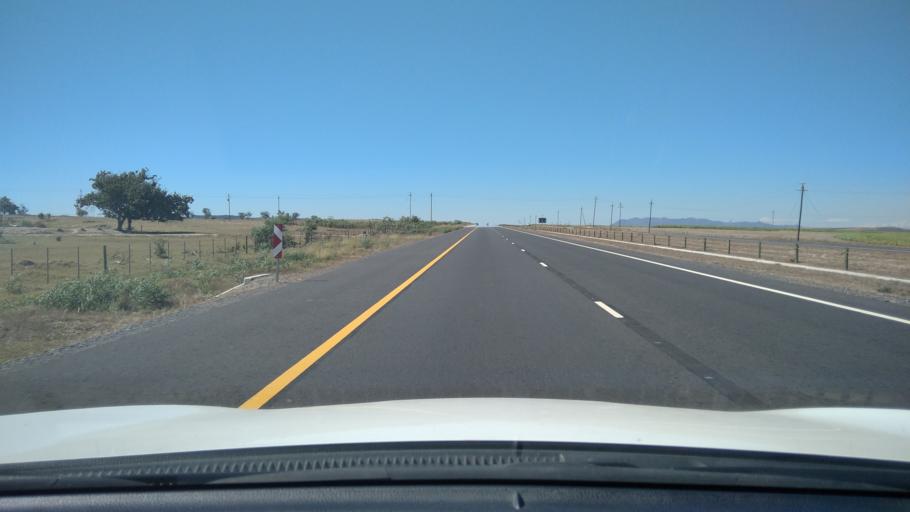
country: ZA
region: Western Cape
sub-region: West Coast District Municipality
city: Malmesbury
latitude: -33.5576
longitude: 18.6275
